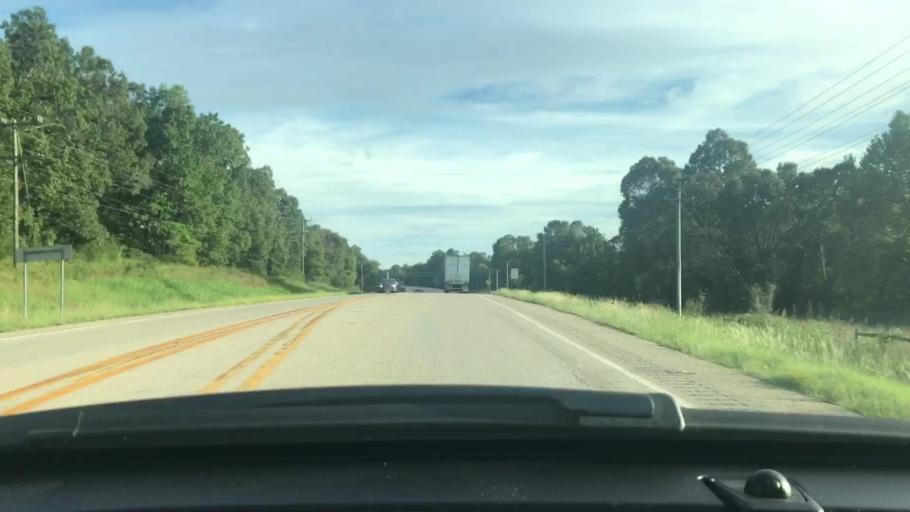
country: US
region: Arkansas
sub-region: Lawrence County
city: Hoxie
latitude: 36.1344
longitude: -91.1583
